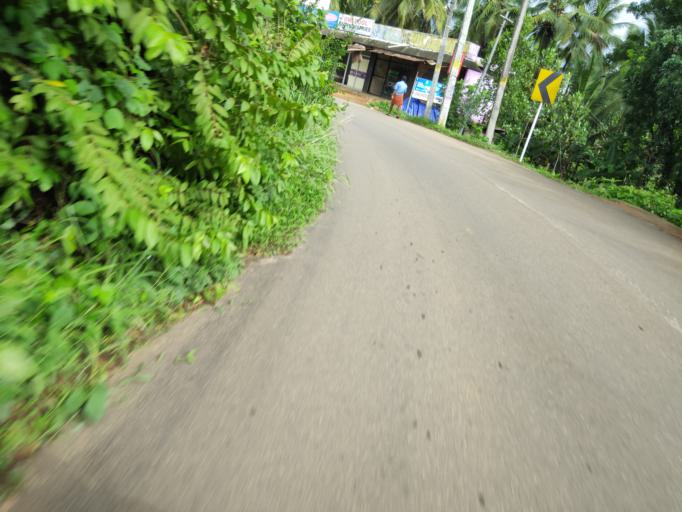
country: IN
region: Kerala
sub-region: Malappuram
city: Manjeri
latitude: 11.1439
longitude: 76.1395
